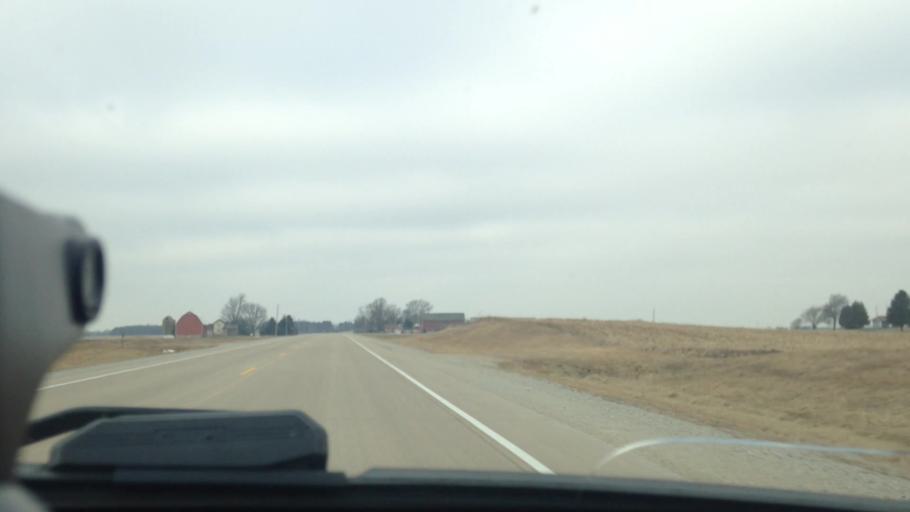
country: US
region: Wisconsin
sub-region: Dodge County
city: Juneau
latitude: 43.4734
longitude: -88.7402
